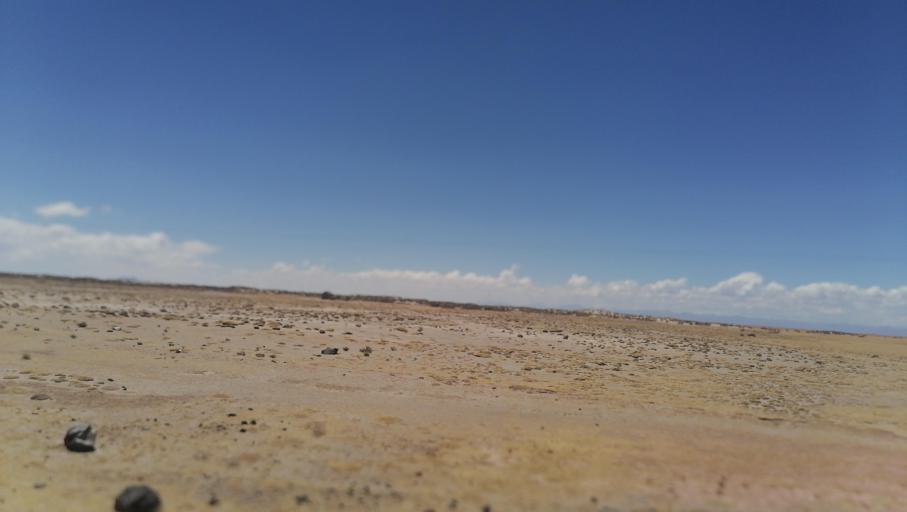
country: BO
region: Oruro
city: Challapata
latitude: -19.2225
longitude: -66.9775
